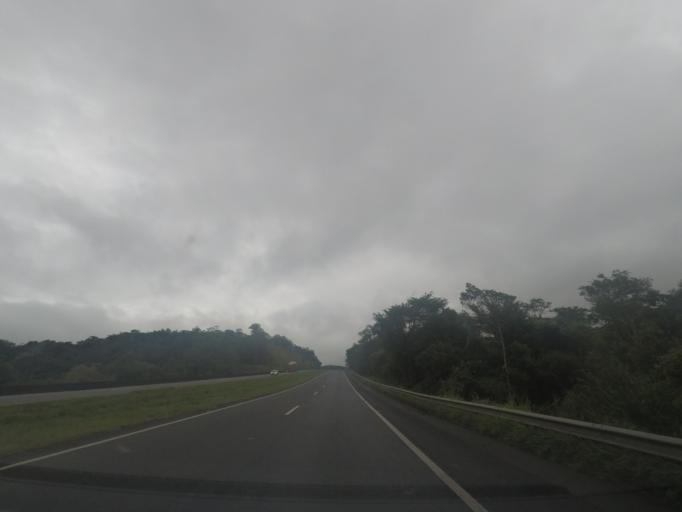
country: BR
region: Parana
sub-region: Antonina
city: Antonina
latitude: -25.0929
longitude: -48.6496
